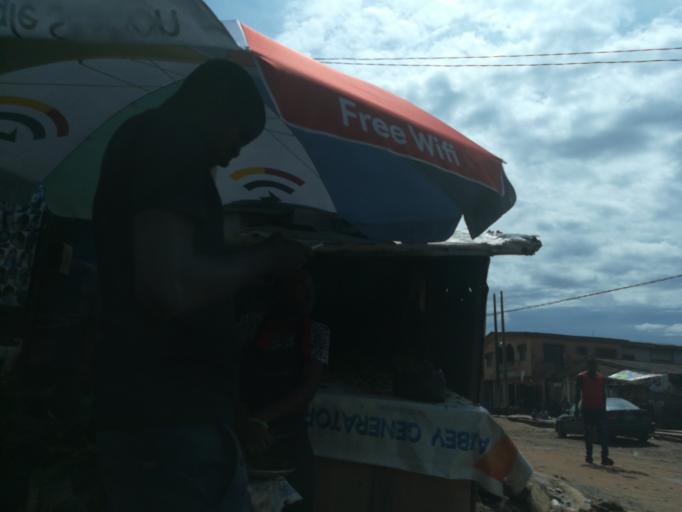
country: NG
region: Lagos
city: Agege
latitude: 6.6069
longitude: 3.3164
